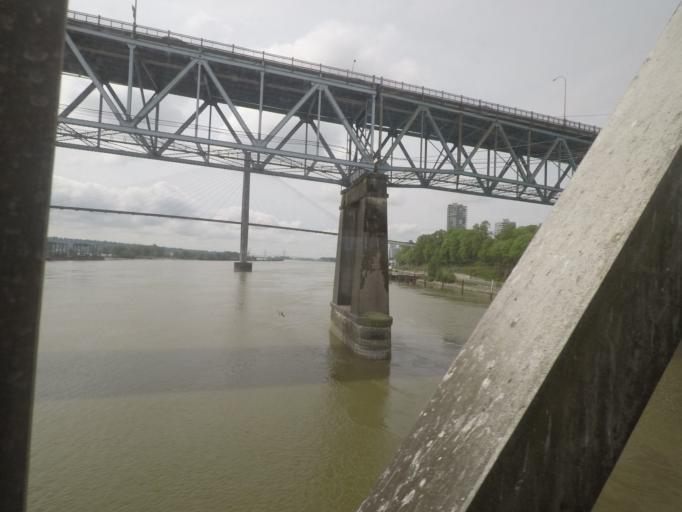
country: CA
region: British Columbia
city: New Westminster
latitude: 49.2086
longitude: -122.8954
